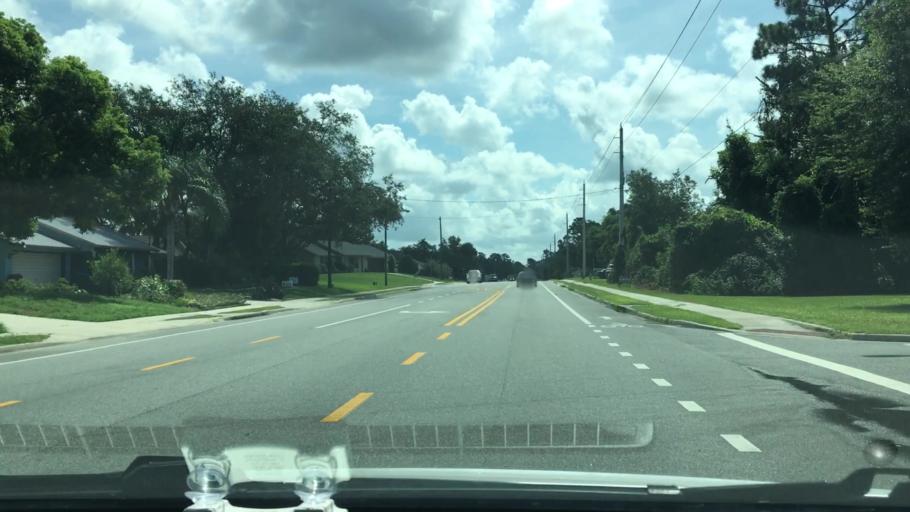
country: US
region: Florida
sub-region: Volusia County
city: Deltona
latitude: 28.8773
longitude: -81.1924
